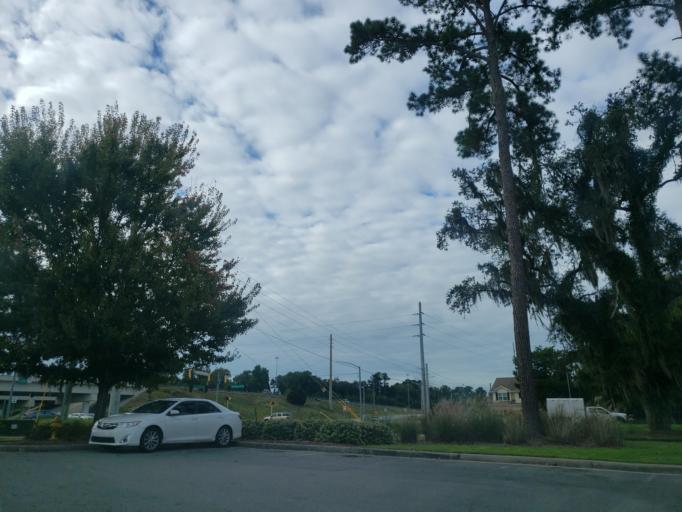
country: US
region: Georgia
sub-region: Chatham County
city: Isle of Hope
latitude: 31.9894
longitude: -81.0820
